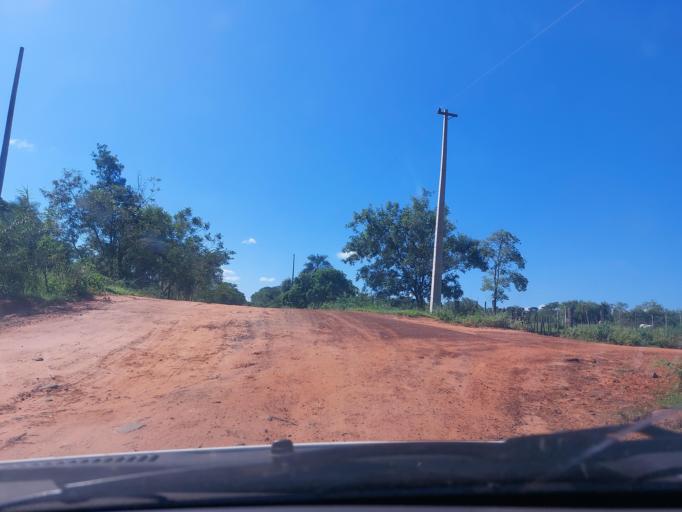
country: PY
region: San Pedro
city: Itacurubi del Rosario
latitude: -24.5483
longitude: -56.5861
